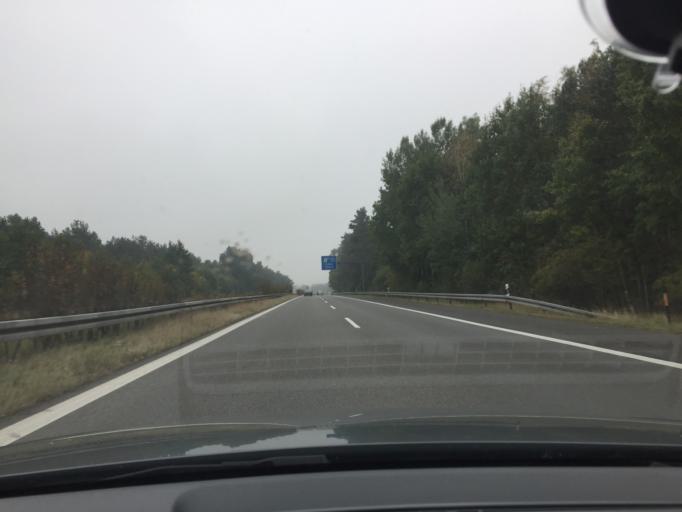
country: DE
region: Brandenburg
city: Calau
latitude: 51.7976
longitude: 13.8831
